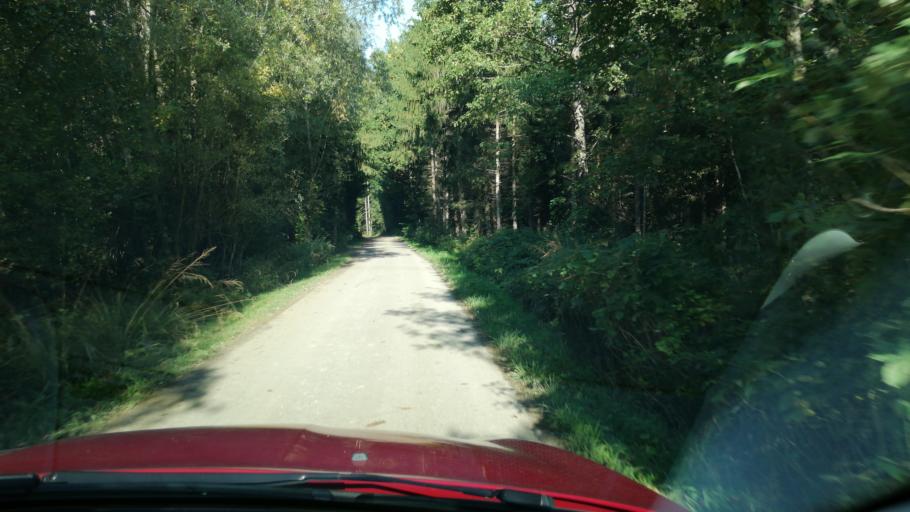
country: AT
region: Upper Austria
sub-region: Politischer Bezirk Kirchdorf an der Krems
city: Kremsmunster
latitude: 48.1016
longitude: 14.1569
